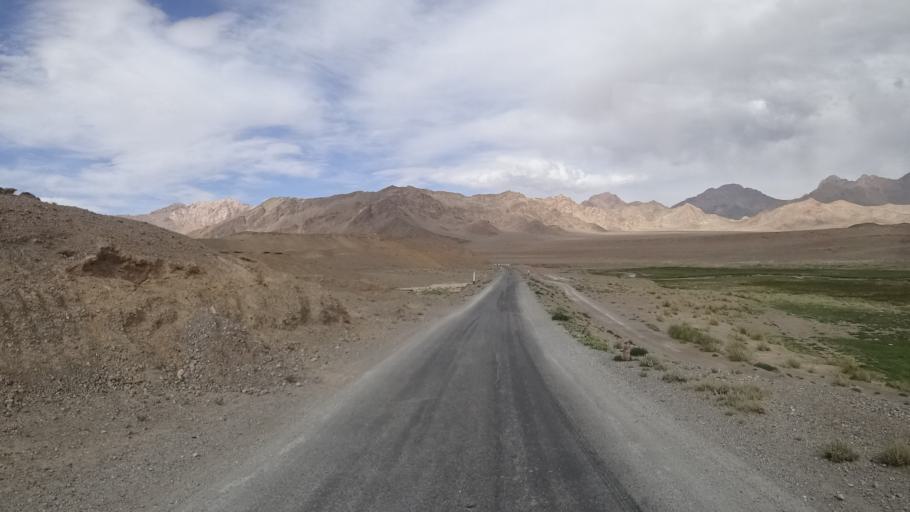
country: TJ
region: Gorno-Badakhshan
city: Murghob
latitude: 38.0233
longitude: 73.9396
